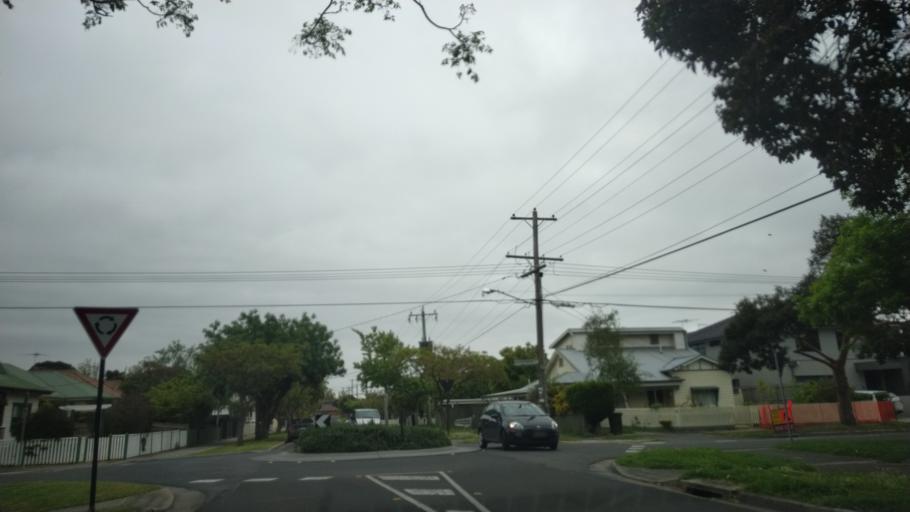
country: AU
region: Victoria
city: Hughesdale
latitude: -37.9030
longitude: 145.0814
